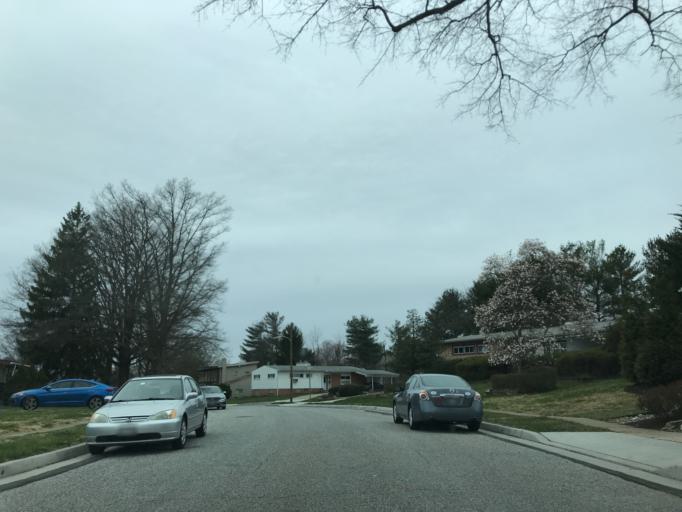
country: US
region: Maryland
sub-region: Baltimore County
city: Pikesville
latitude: 39.3791
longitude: -76.6813
